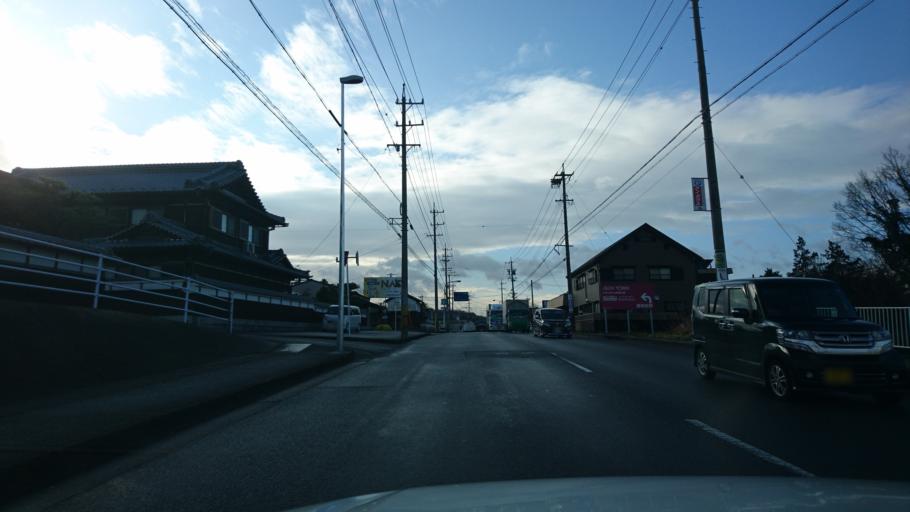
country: JP
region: Mie
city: Ueno-ebisumachi
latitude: 34.7583
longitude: 136.1238
